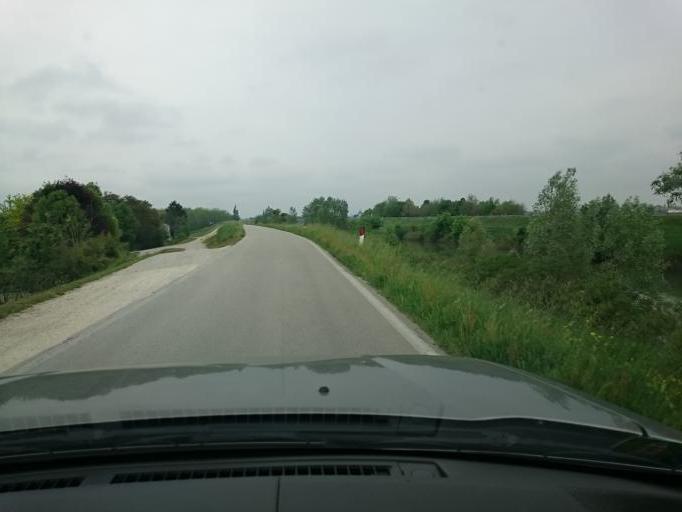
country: IT
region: Veneto
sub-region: Provincia di Padova
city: Bovolenta
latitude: 45.2630
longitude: 11.9654
